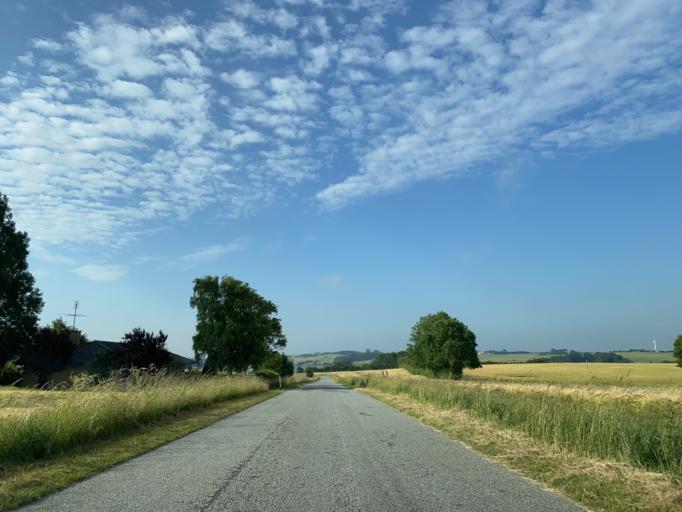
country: DK
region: South Denmark
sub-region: Haderslev Kommune
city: Haderslev
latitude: 55.1783
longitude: 9.4815
